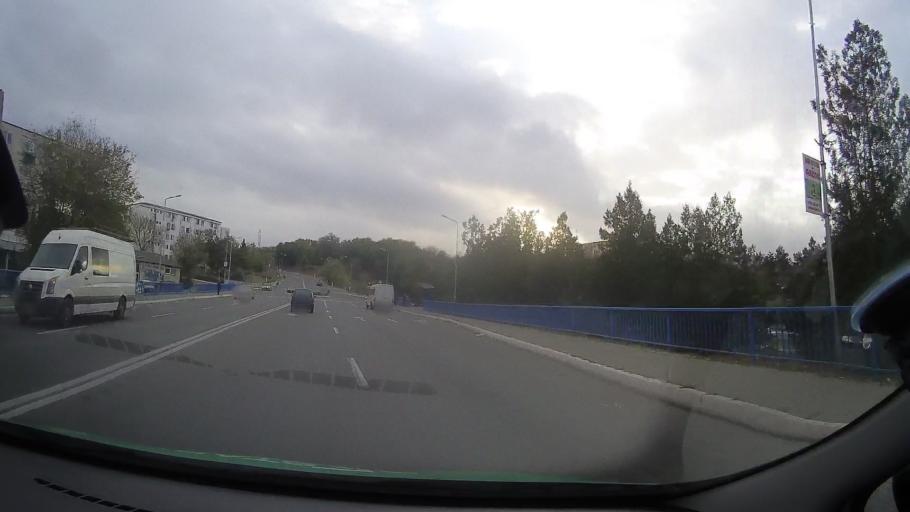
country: RO
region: Constanta
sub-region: Municipiul Medgidia
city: Medgidia
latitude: 44.2476
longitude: 28.2606
